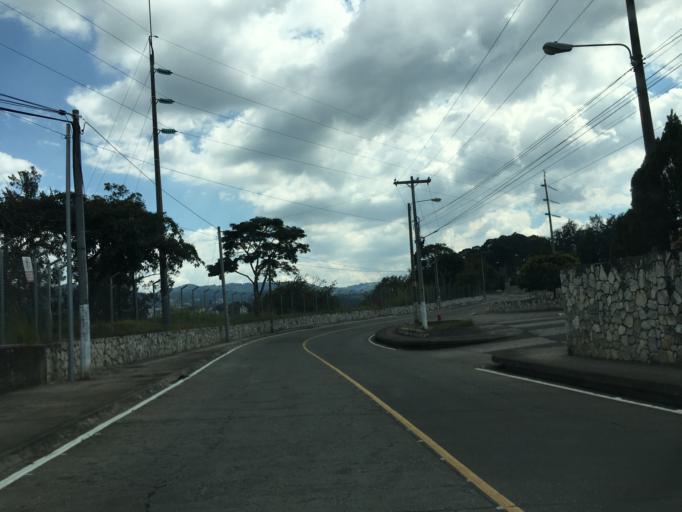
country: GT
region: Guatemala
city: Guatemala City
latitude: 14.6279
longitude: -90.4610
